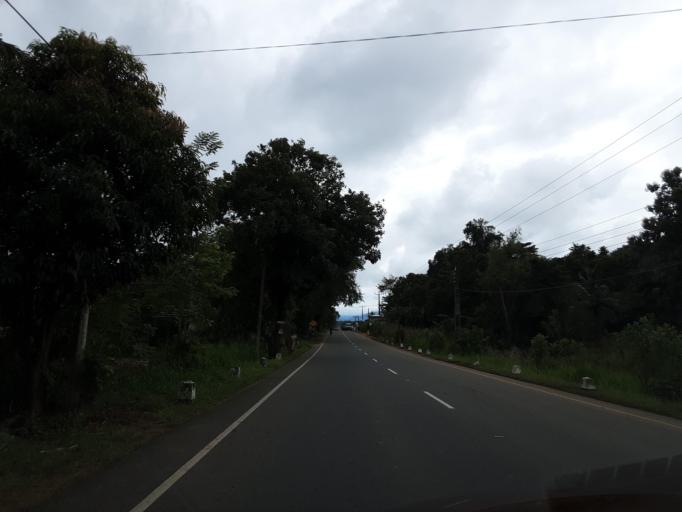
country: LK
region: Uva
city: Badulla
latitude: 7.3799
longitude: 81.0706
